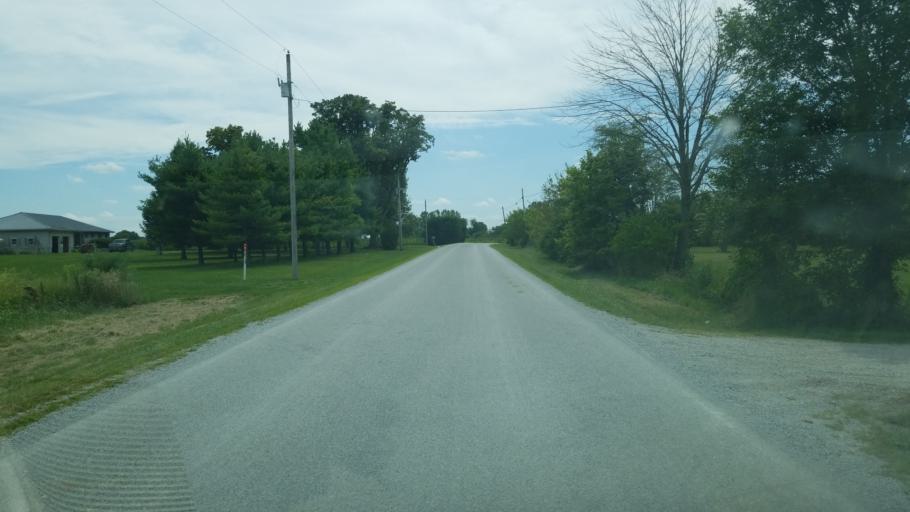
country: US
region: Ohio
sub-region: Hardin County
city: Kenton
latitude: 40.5743
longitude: -83.5051
